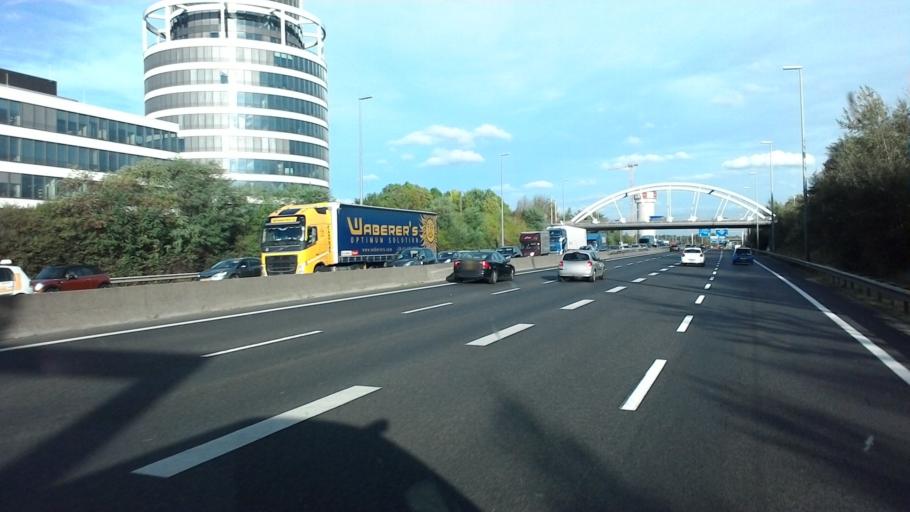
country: LU
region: Luxembourg
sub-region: Canton de Luxembourg
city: Luxembourg
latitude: 49.5783
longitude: 6.1096
